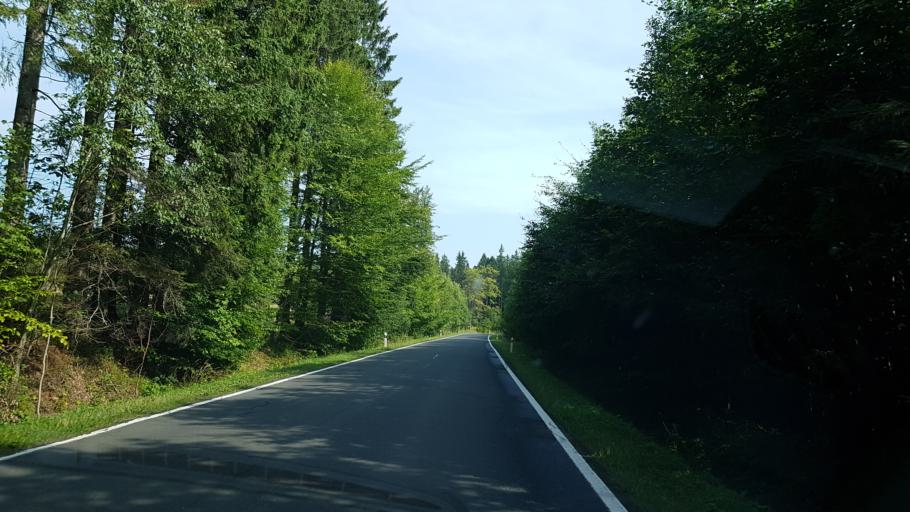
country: CZ
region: Olomoucky
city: Pisecna
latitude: 50.2231
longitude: 17.2732
